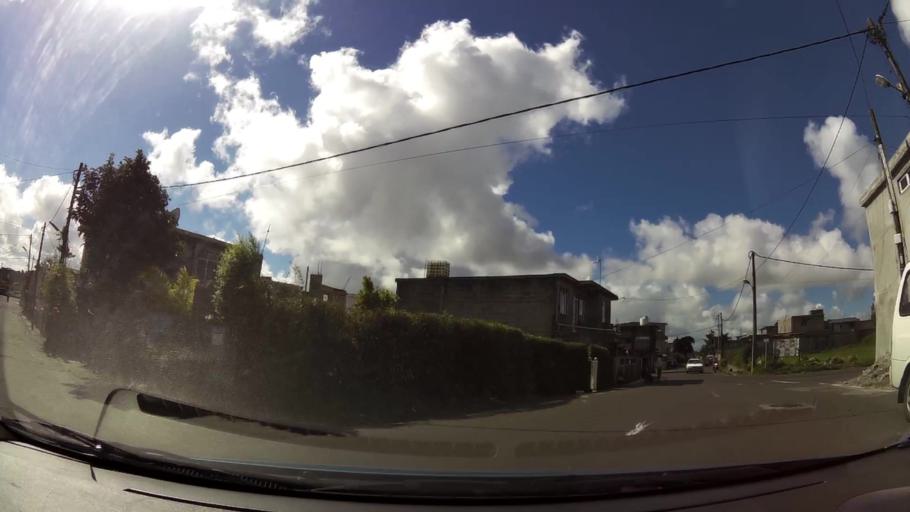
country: MU
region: Plaines Wilhems
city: Curepipe
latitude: -20.3305
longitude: 57.5212
